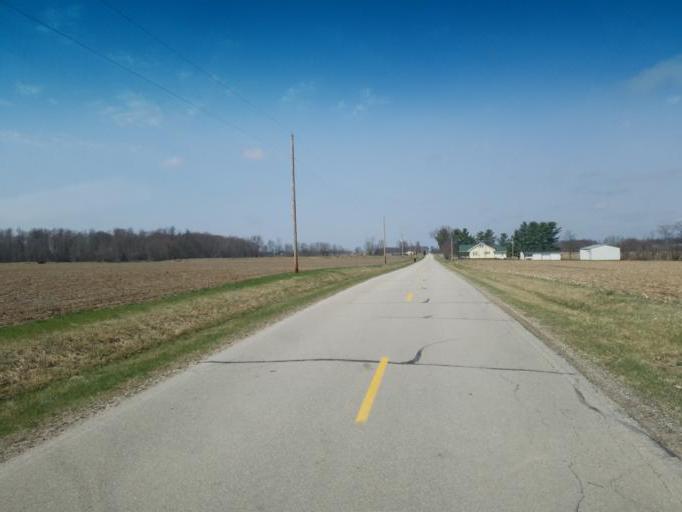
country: US
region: Ohio
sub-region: Crawford County
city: Bucyrus
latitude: 40.9065
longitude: -83.1006
